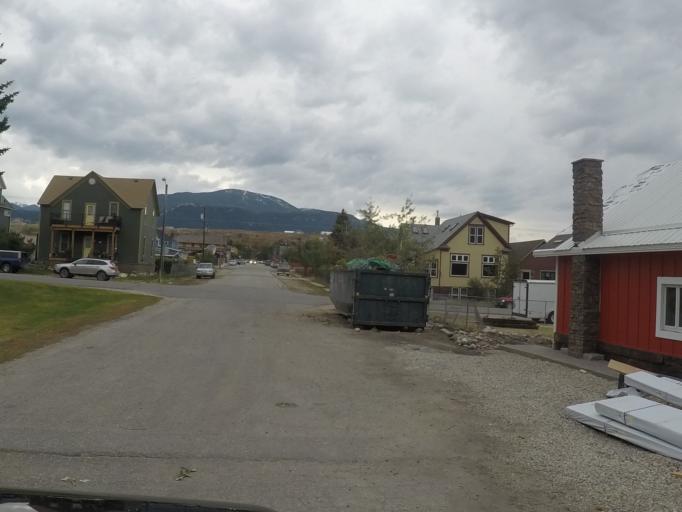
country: US
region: Montana
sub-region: Carbon County
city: Red Lodge
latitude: 45.1850
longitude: -109.2438
